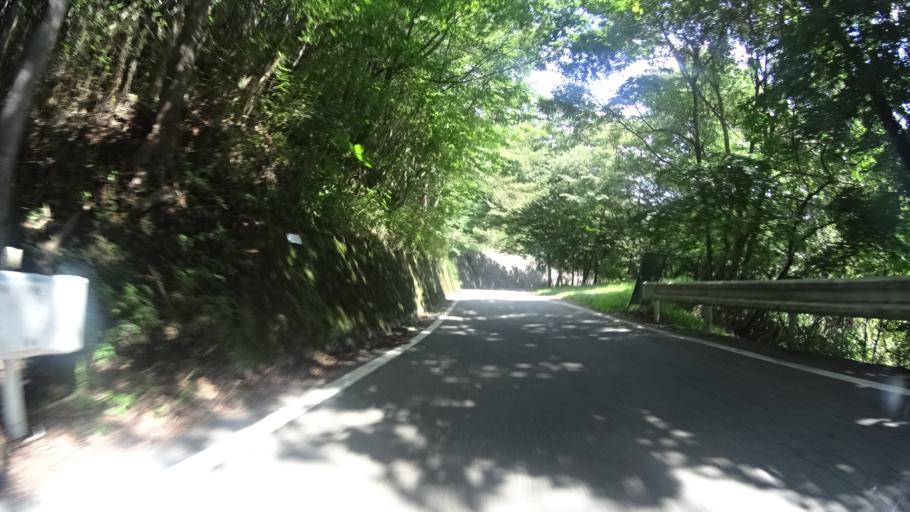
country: JP
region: Yamanashi
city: Enzan
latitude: 35.7988
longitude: 138.6817
